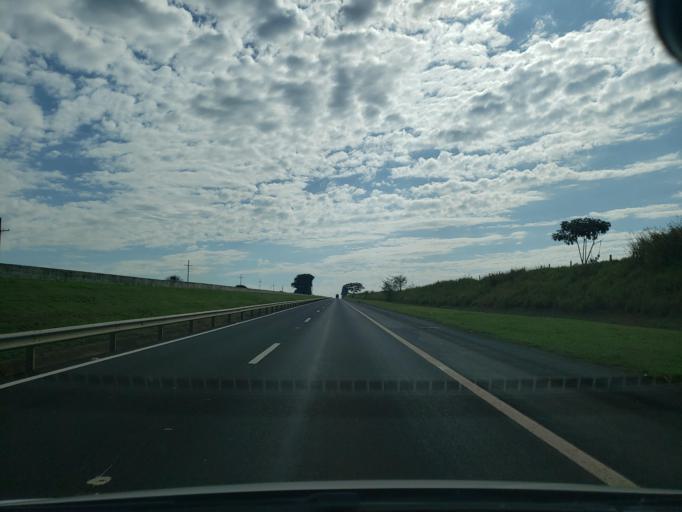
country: BR
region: Sao Paulo
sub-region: Lins
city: Lins
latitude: -21.6435
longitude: -49.8216
